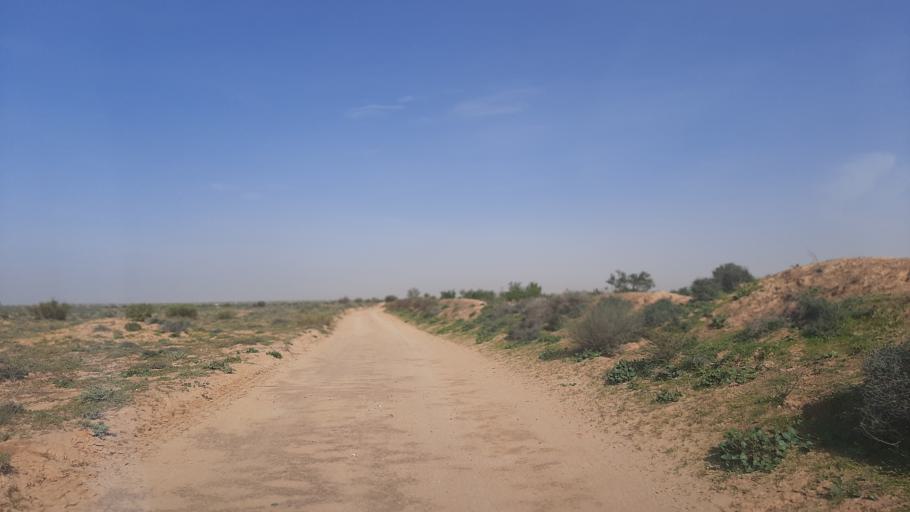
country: TN
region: Madanin
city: Zarzis
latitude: 33.4413
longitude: 10.8076
